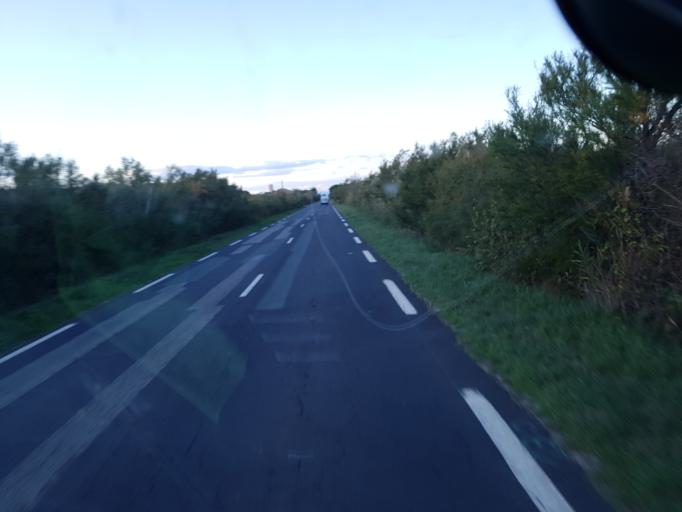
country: FR
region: Languedoc-Roussillon
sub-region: Departement de l'Aude
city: Port-la-Nouvelle
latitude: 43.0020
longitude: 3.0404
